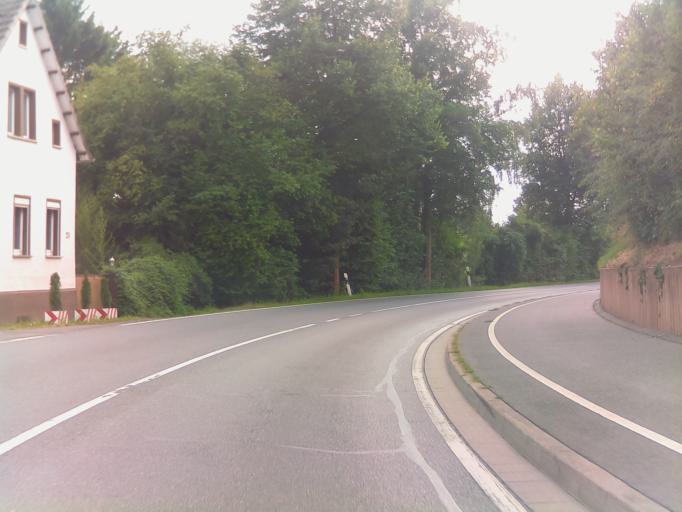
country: DE
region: Hesse
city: Ober-Ramstadt
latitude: 49.8194
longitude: 8.6970
